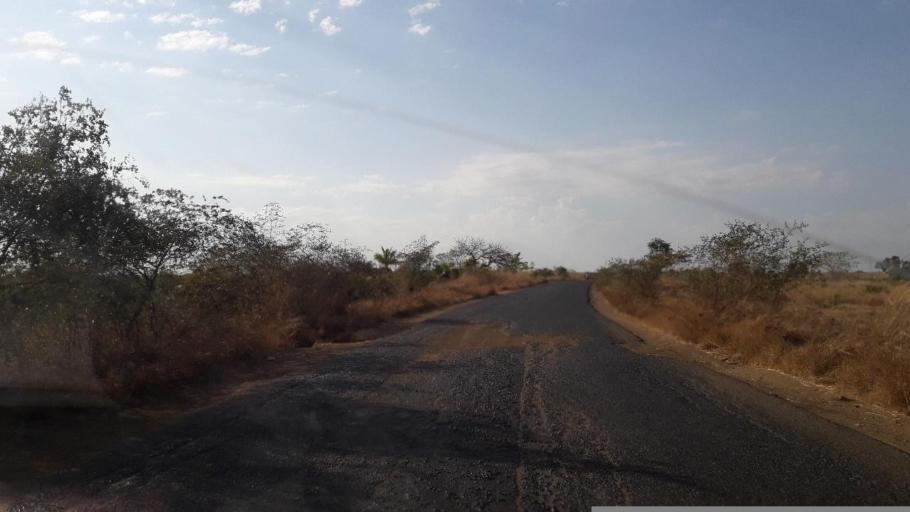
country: MG
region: Boeny
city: Mahajanga
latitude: -15.8607
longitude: 46.5220
